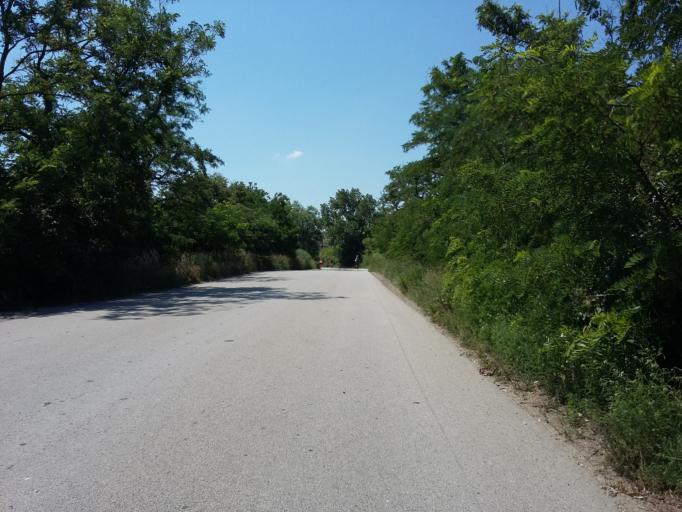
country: AT
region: Lower Austria
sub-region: Politischer Bezirk Ganserndorf
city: Marchegg
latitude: 48.2977
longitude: 16.9691
